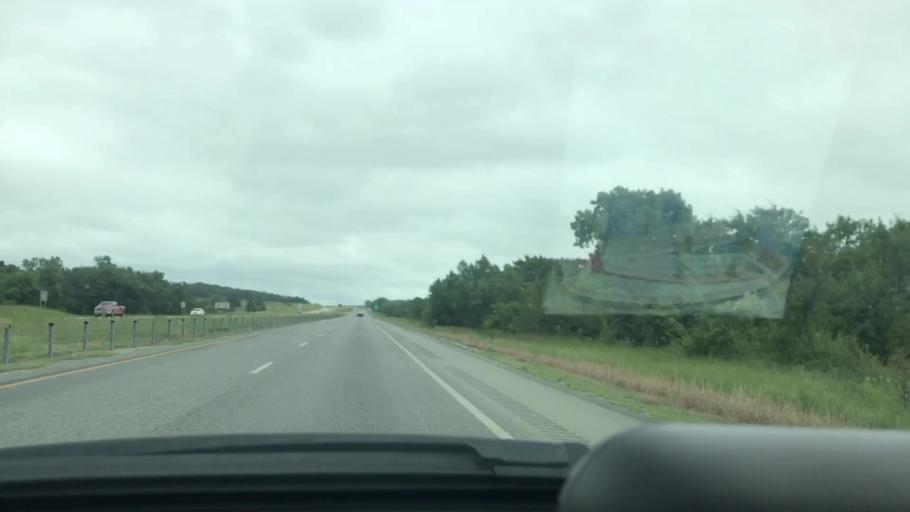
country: US
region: Oklahoma
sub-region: Coal County
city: Coalgate
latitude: 34.6609
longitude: -95.9394
